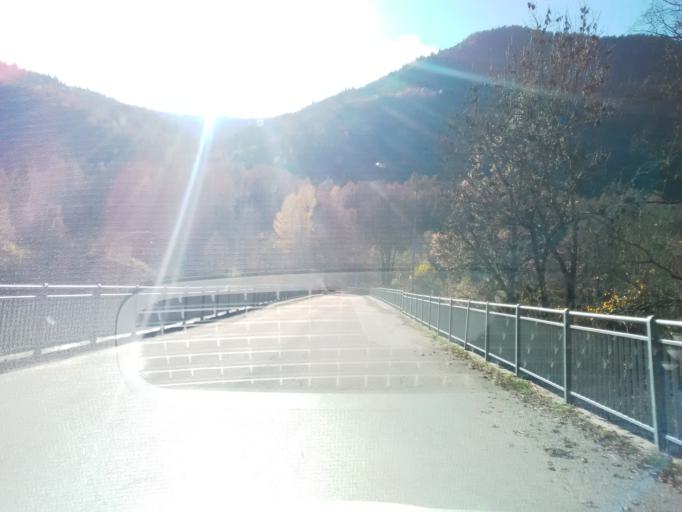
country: IT
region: Piedmont
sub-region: Provincia di Vercelli
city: Pila
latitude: 45.7693
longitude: 8.0775
